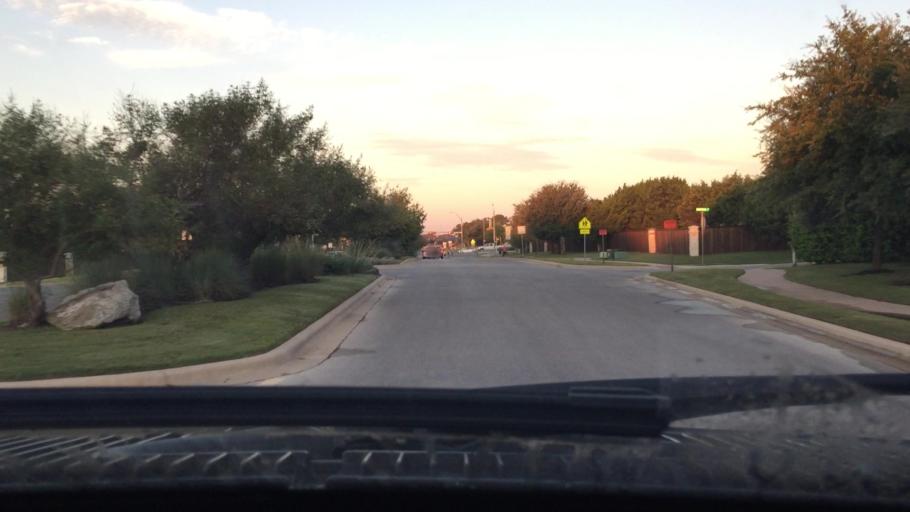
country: US
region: Texas
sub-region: Williamson County
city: Leander
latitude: 30.5388
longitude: -97.8596
